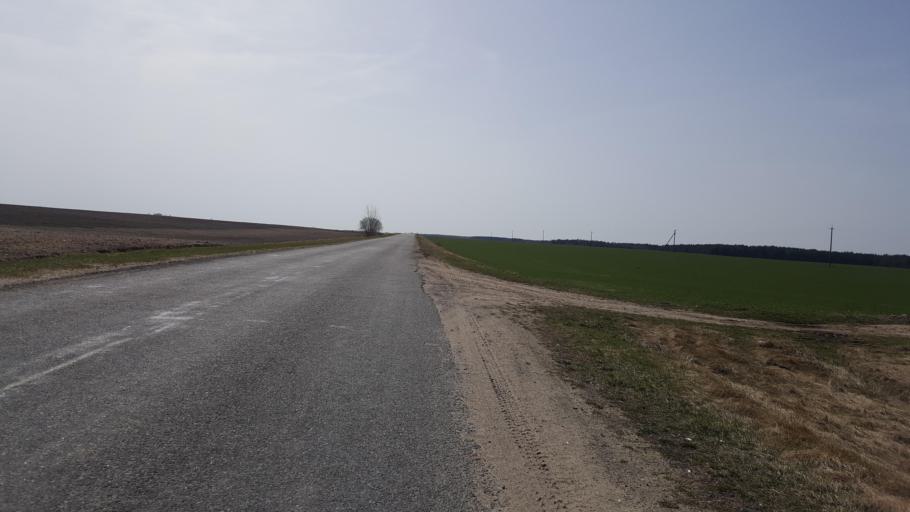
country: BY
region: Brest
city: Kamyanyets
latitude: 52.4769
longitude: 23.8692
